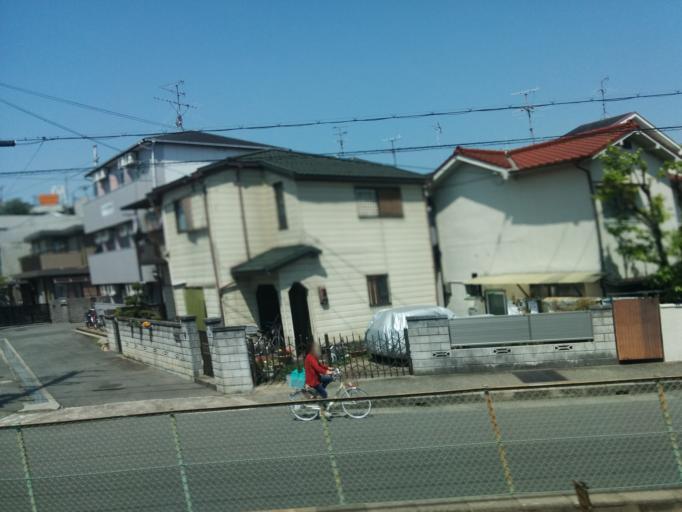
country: JP
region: Osaka
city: Ibaraki
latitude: 34.8290
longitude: 135.5862
